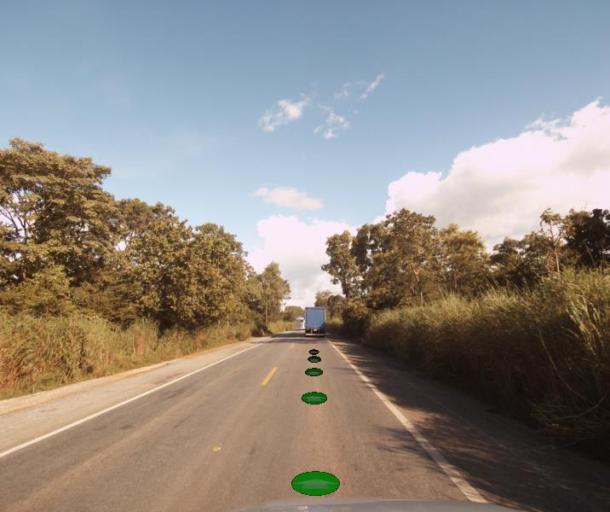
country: BR
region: Goias
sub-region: Porangatu
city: Porangatu
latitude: -13.1228
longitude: -49.1981
